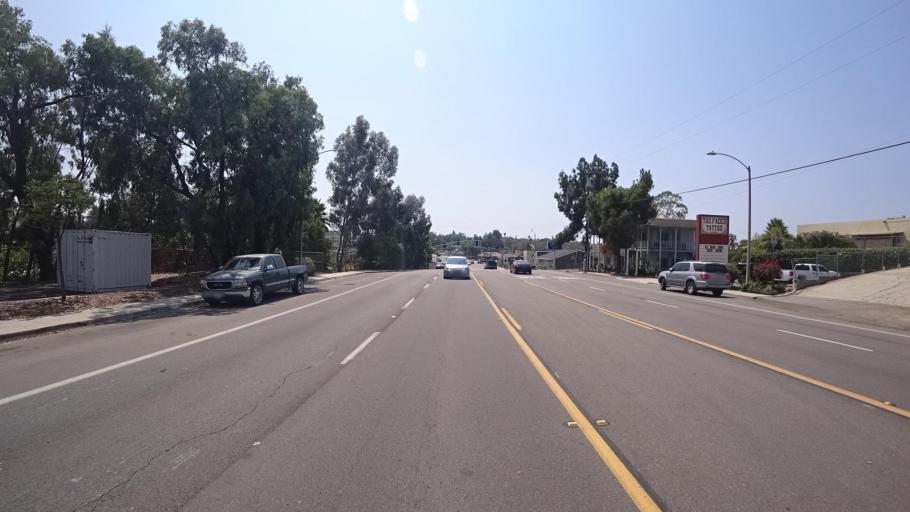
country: US
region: California
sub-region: San Diego County
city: Fallbrook
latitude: 33.3748
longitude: -117.2536
